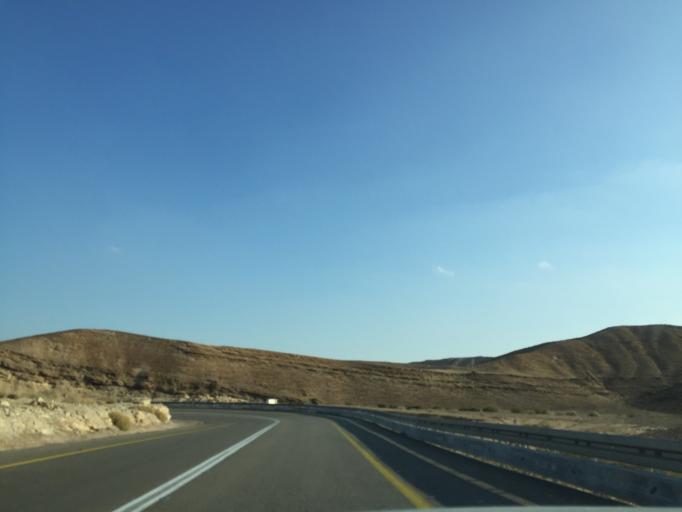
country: IL
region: Southern District
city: `En Boqeq
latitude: 31.1751
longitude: 35.2978
